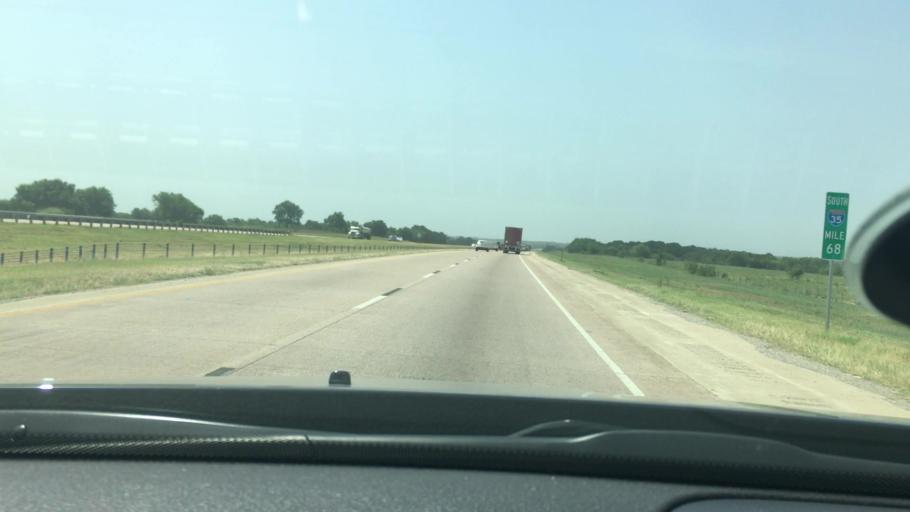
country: US
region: Oklahoma
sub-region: Garvin County
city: Pauls Valley
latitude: 34.6811
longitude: -97.2282
